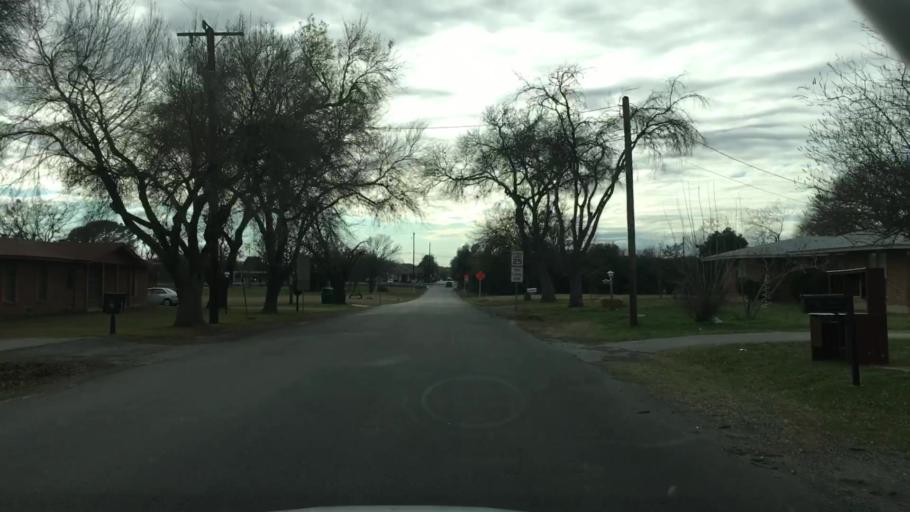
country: US
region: Texas
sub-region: Bexar County
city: Converse
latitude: 29.5175
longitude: -98.3102
